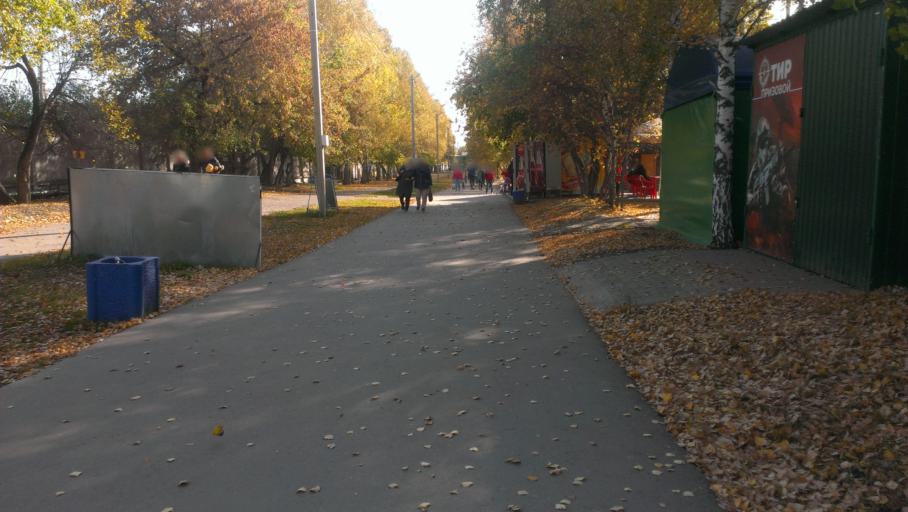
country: RU
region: Altai Krai
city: Novosilikatnyy
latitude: 53.3575
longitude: 83.6847
